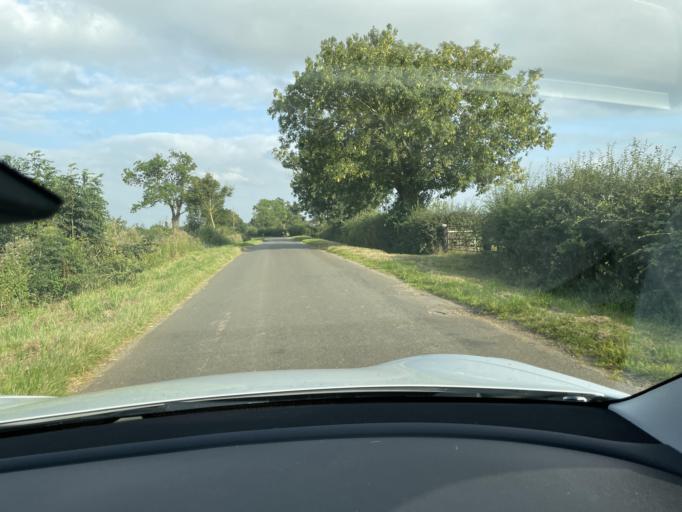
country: GB
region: England
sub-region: Northamptonshire
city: Long Buckby
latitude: 52.4199
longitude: -1.0419
